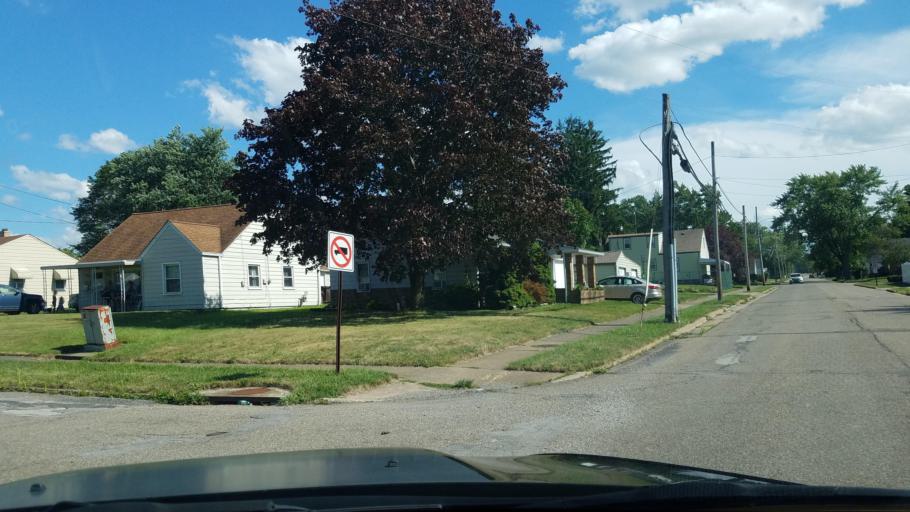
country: US
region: Ohio
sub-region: Mahoning County
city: Struthers
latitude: 41.0597
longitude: -80.6263
